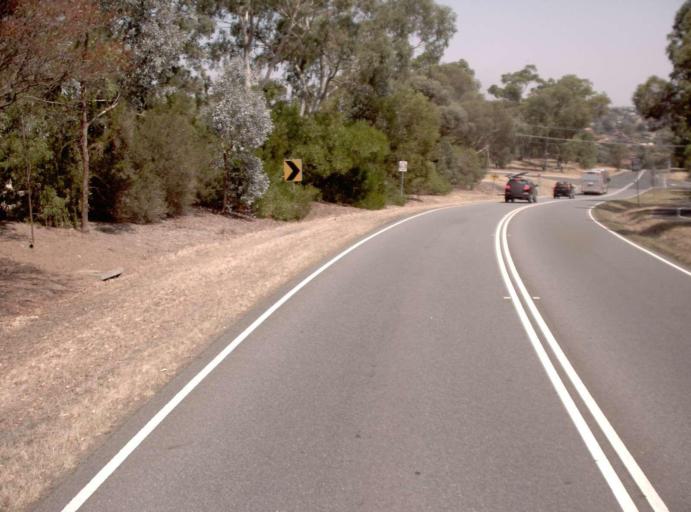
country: AU
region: Victoria
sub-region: Manningham
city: Doncaster East
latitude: -37.7734
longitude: 145.1421
